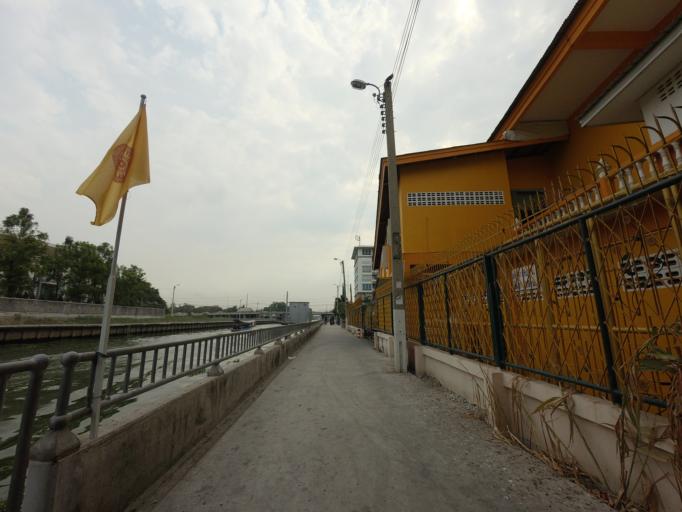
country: TH
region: Bangkok
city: Suan Luang
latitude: 13.7154
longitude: 100.6412
